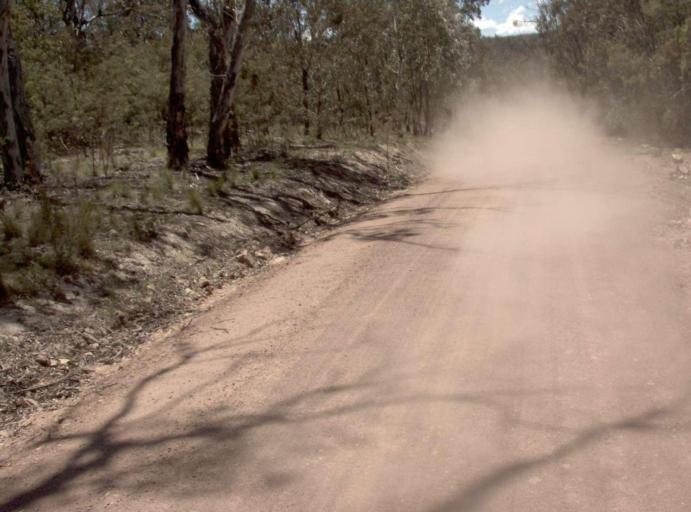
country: AU
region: New South Wales
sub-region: Snowy River
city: Jindabyne
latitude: -37.0656
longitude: 148.3186
